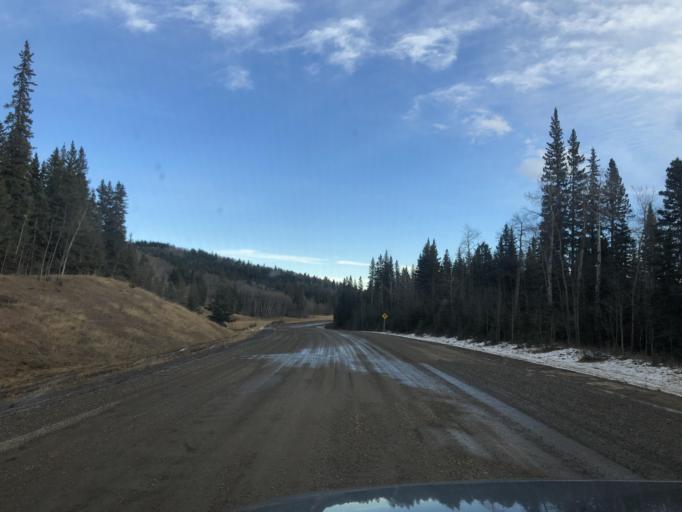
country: CA
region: Alberta
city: Cochrane
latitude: 51.0413
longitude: -114.7462
